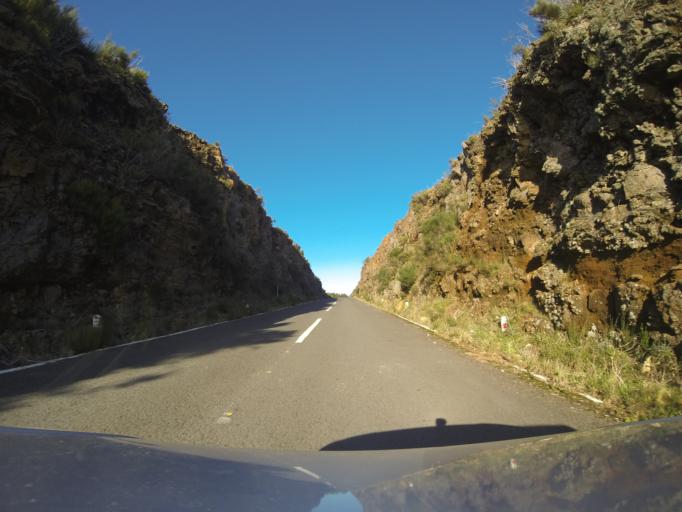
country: PT
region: Madeira
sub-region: Sao Vicente
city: Sao Vicente
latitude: 32.7665
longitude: -17.0775
